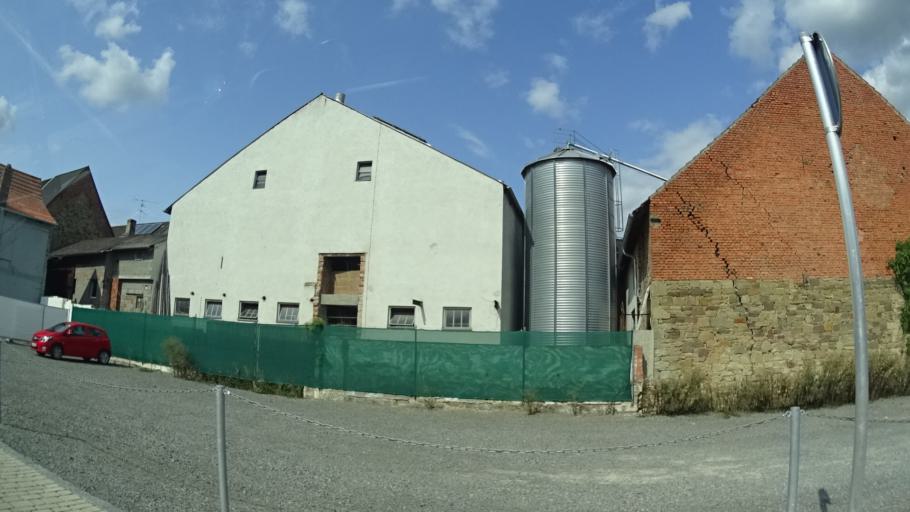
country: DE
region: Bavaria
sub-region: Regierungsbezirk Unterfranken
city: Bergrheinfeld
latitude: 50.0060
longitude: 10.1816
